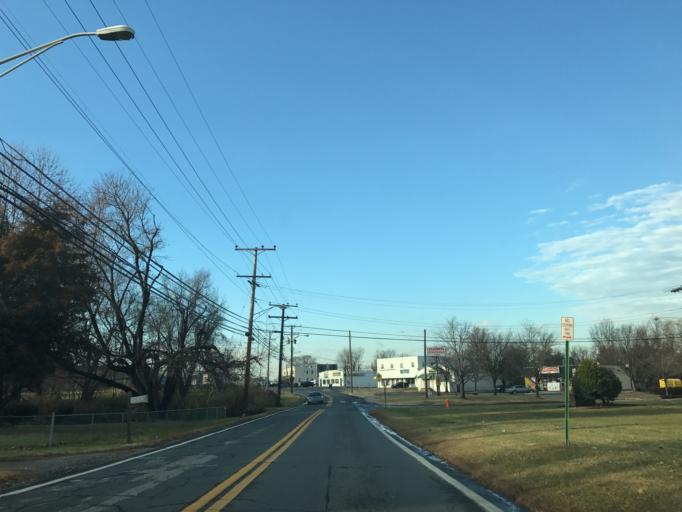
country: US
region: Maryland
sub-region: Baltimore County
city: Edgemere
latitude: 39.2384
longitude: -76.4435
